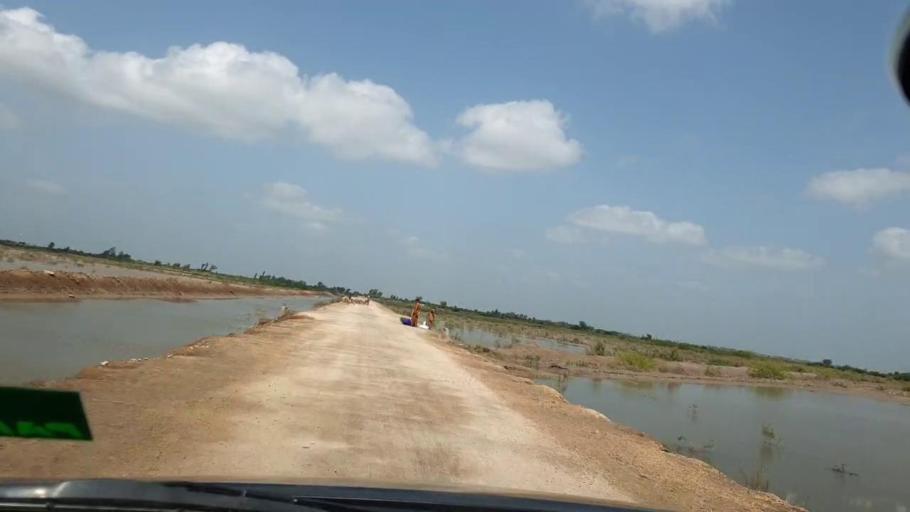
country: PK
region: Sindh
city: Kadhan
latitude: 24.5974
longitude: 69.1280
